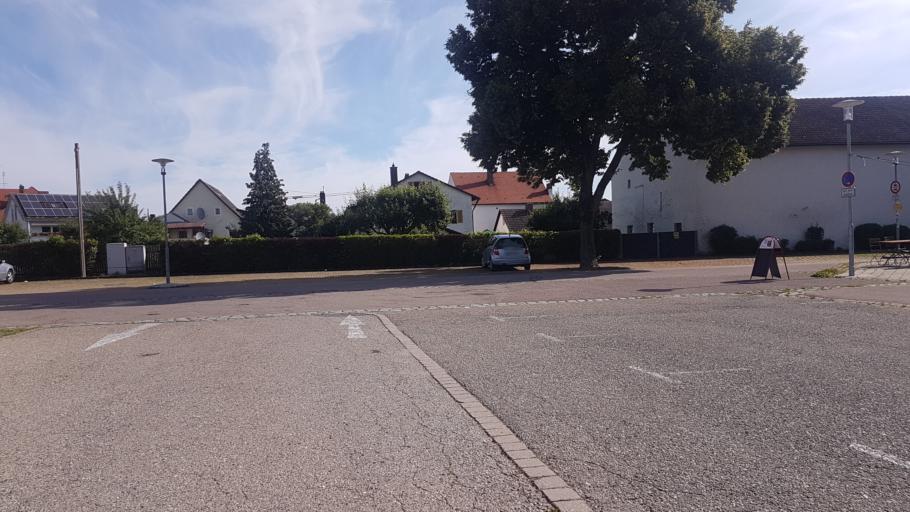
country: DE
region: Bavaria
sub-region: Regierungsbezirk Mittelfranken
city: Treuchtlingen
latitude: 48.9535
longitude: 10.9127
